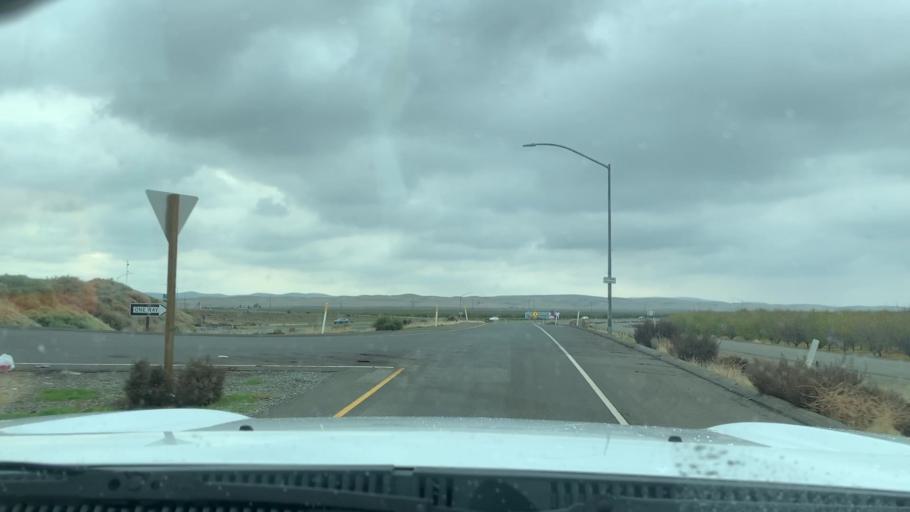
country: US
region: California
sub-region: Kings County
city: Kettleman City
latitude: 35.9347
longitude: -119.9105
